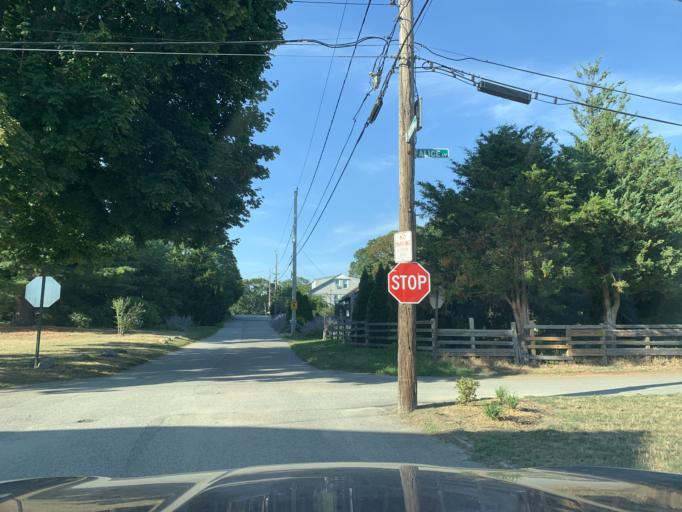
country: US
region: Rhode Island
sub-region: Kent County
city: Warwick
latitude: 41.6891
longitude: -71.4410
